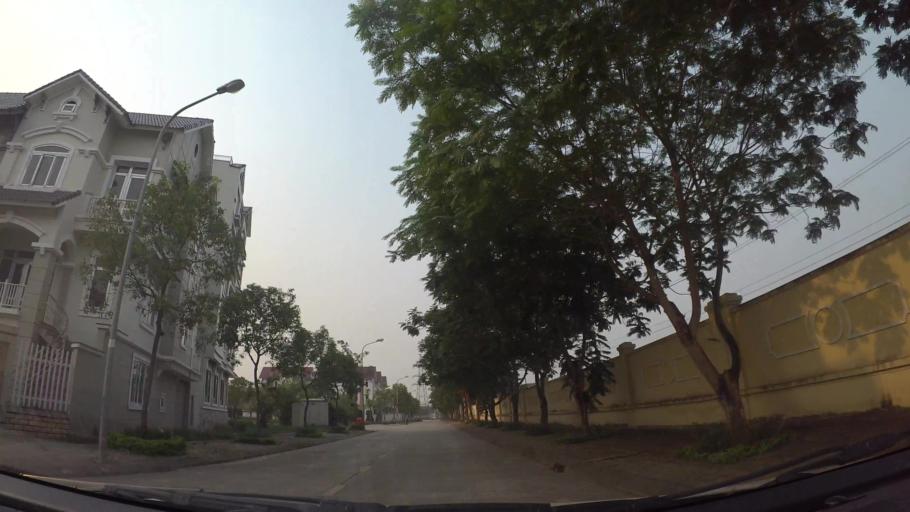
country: VN
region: Ha Noi
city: Cau Dien
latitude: 21.0056
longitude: 105.7343
